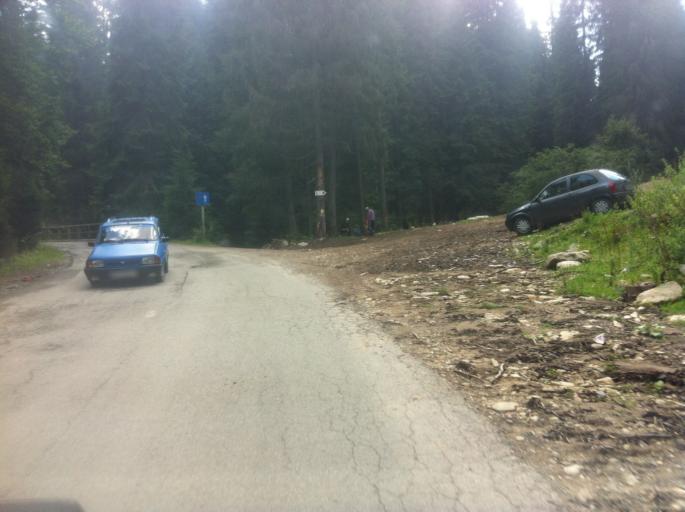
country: RO
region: Hunedoara
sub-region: Oras Petrila
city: Petrila
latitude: 45.4087
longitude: 23.5576
